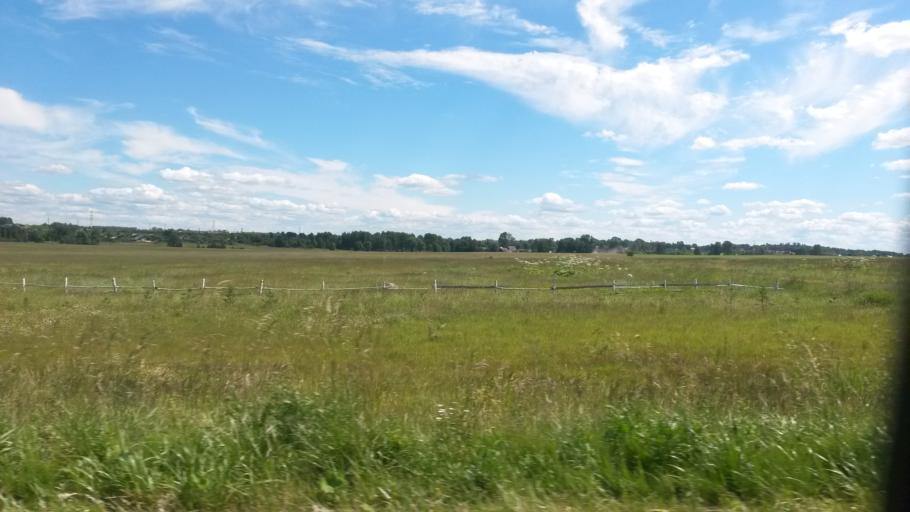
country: RU
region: Ivanovo
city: Staraya Vichuga
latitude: 57.2329
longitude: 41.8725
